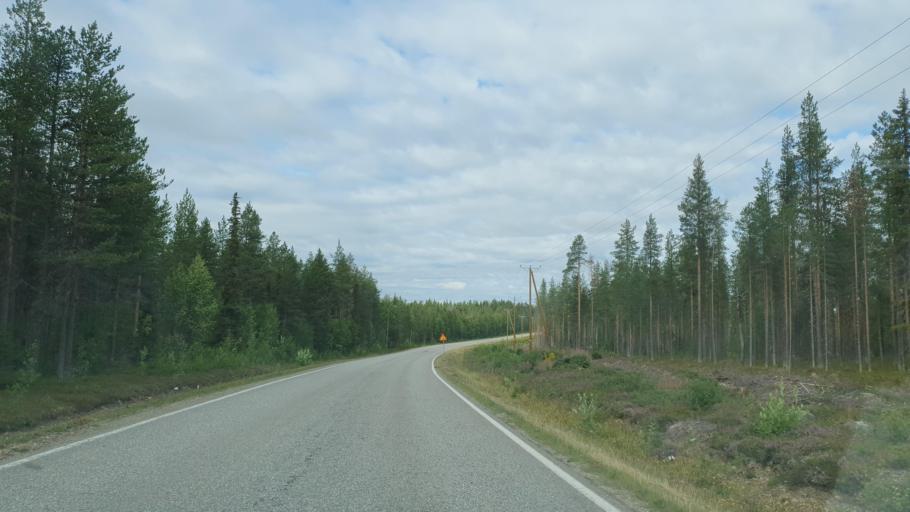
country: FI
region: Lapland
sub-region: Pohjois-Lappi
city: Sodankylae
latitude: 67.4777
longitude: 26.1144
